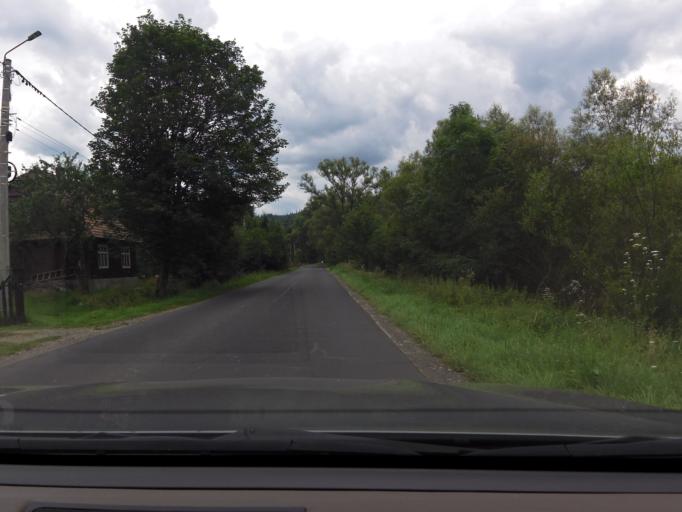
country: PL
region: Silesian Voivodeship
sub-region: Powiat zywiecki
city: Rajcza
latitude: 49.4921
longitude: 19.1211
